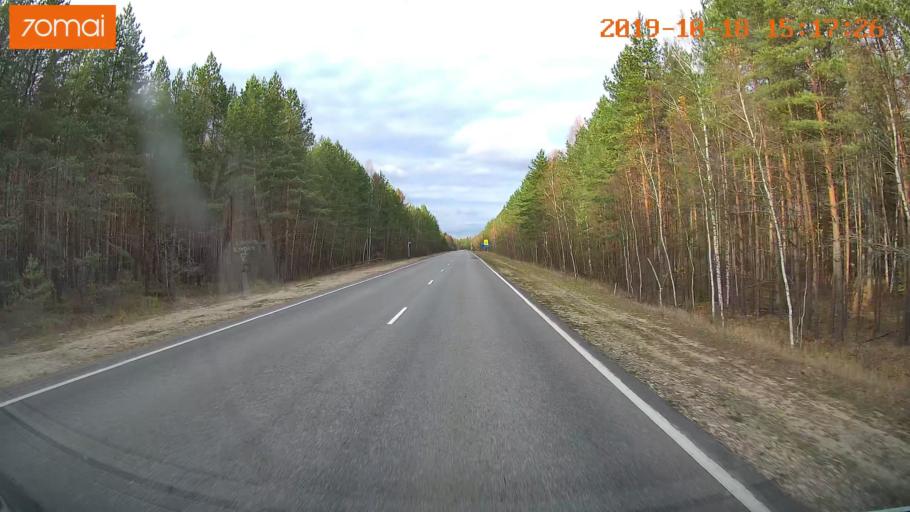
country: RU
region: Vladimir
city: Anopino
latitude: 55.6496
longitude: 40.7265
